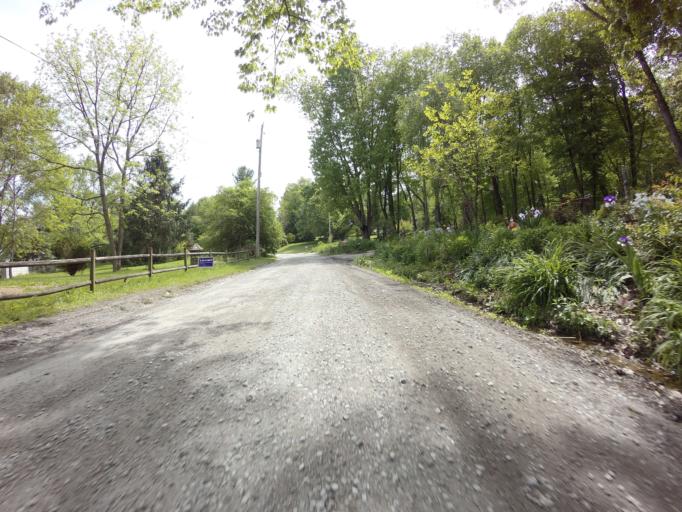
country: US
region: Maryland
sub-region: Carroll County
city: New Windsor
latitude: 39.4938
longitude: -77.0986
